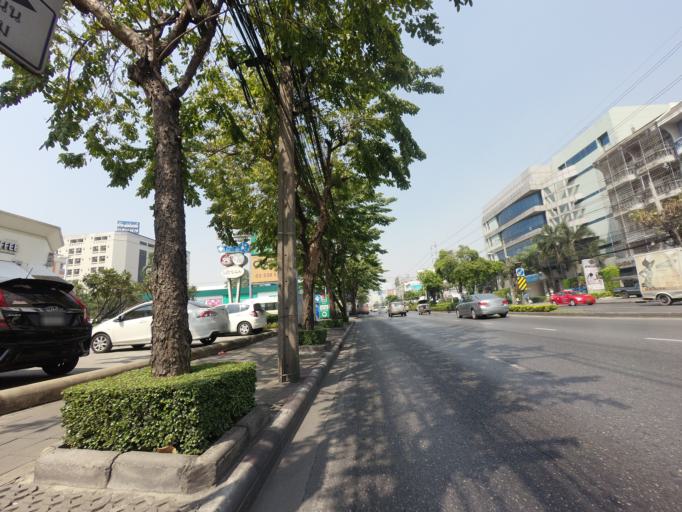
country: TH
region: Bangkok
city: Wang Thonglang
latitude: 13.7781
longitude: 100.6235
